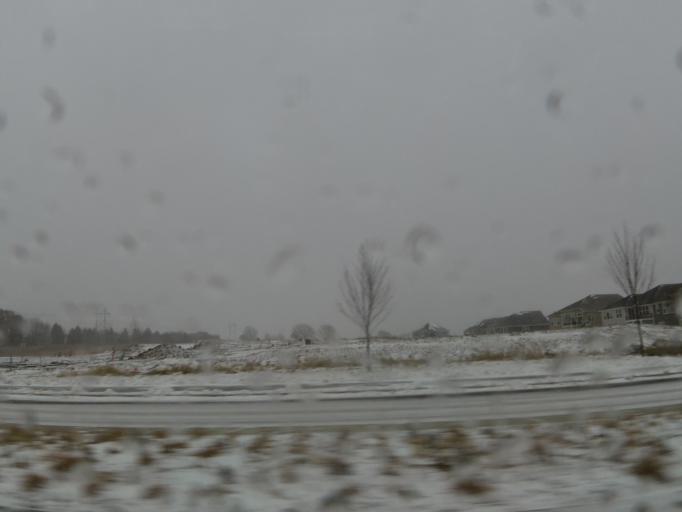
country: US
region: Minnesota
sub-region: Washington County
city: Oakdale
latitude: 44.9550
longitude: -92.9237
